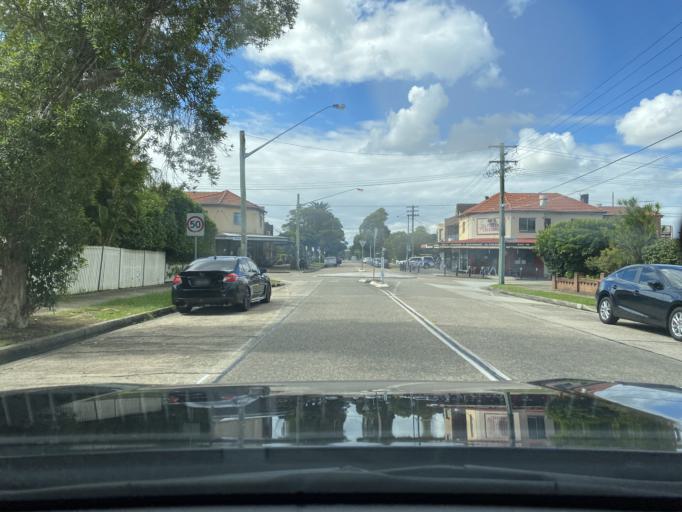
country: AU
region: New South Wales
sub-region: Canada Bay
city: Wareemba
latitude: -33.8664
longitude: 151.1406
